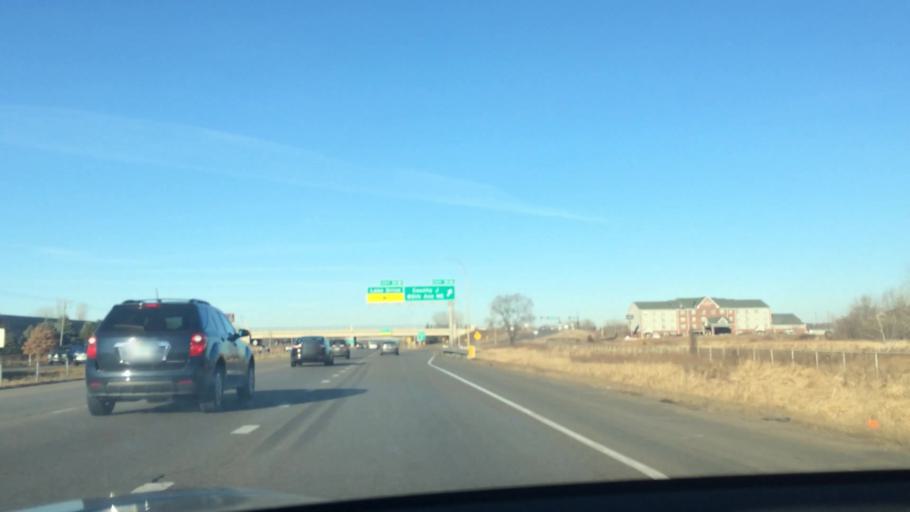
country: US
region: Minnesota
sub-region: Ramsey County
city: Mounds View
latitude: 45.1206
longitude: -93.1883
